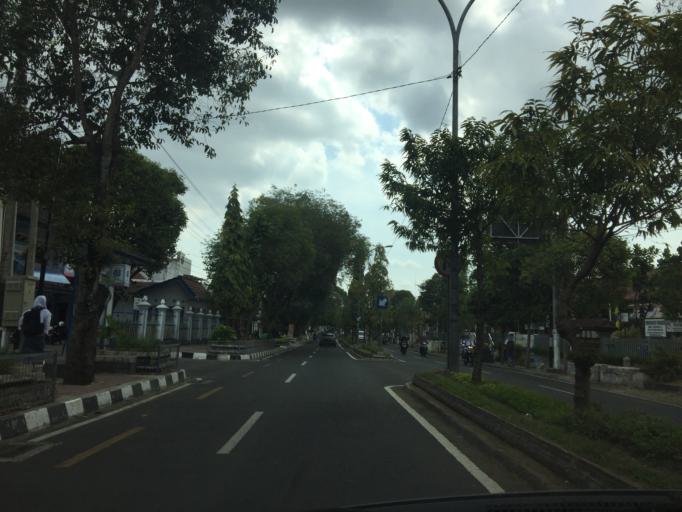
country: ID
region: Daerah Istimewa Yogyakarta
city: Yogyakarta
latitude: -7.7781
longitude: 110.3670
